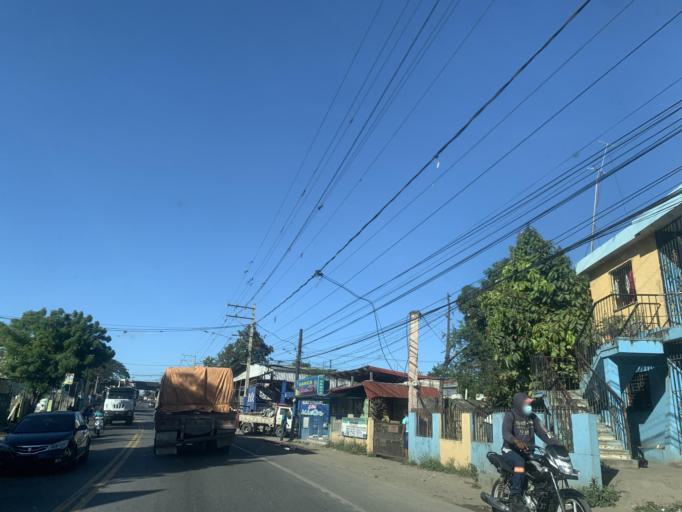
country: DO
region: San Cristobal
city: Bajos de Haina
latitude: 18.4295
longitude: -70.0289
